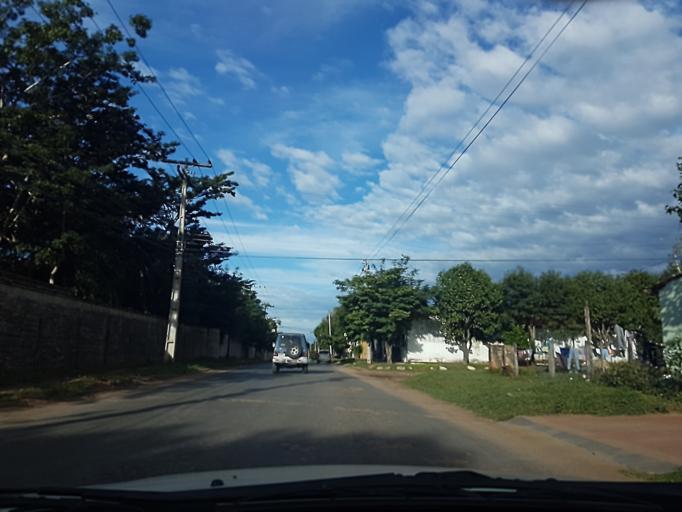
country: PY
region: Central
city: Colonia Mariano Roque Alonso
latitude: -25.2170
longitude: -57.5411
